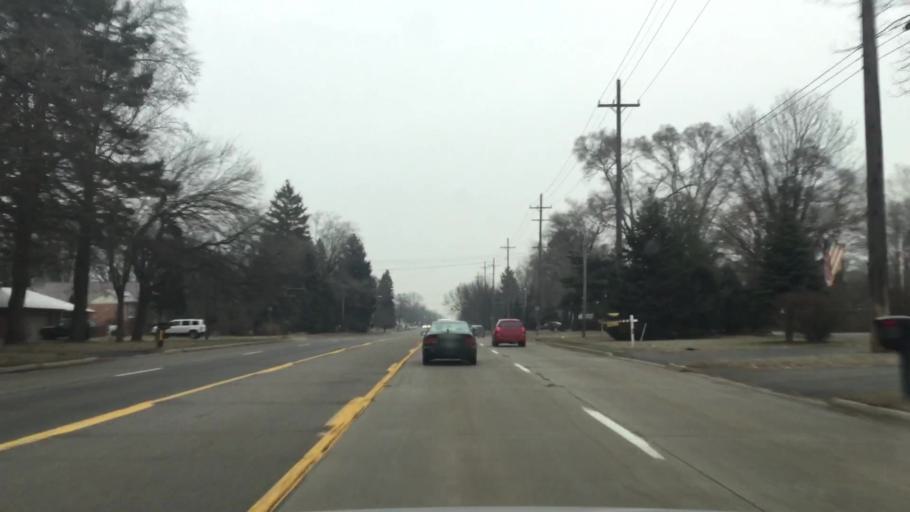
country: US
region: Michigan
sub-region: Oakland County
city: Farmington
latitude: 42.4219
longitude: -83.3551
